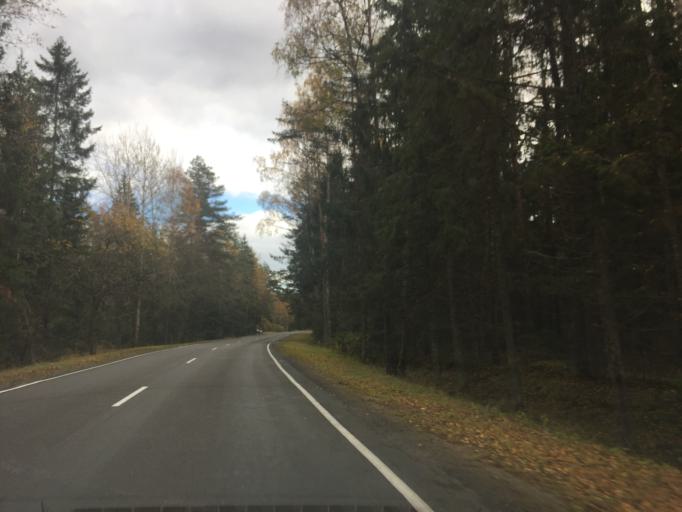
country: BY
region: Minsk
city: Svir
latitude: 54.9250
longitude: 26.4985
